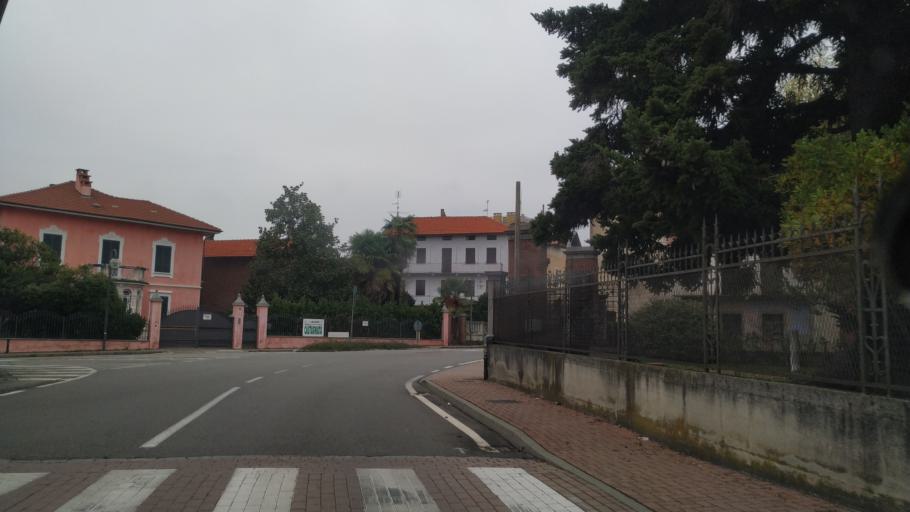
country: IT
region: Piedmont
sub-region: Provincia di Biella
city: Lessona
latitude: 45.5876
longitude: 8.1930
